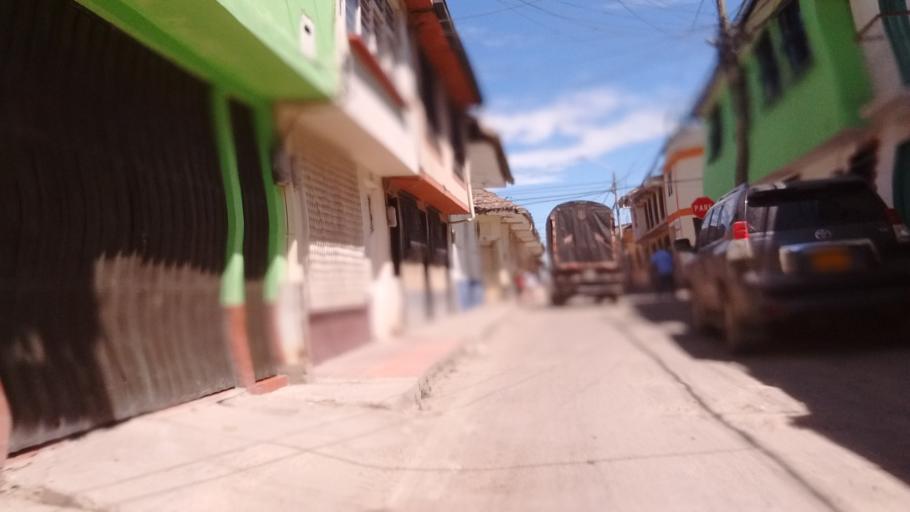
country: CO
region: Cauca
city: Popayan
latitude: 2.4367
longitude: -76.6065
